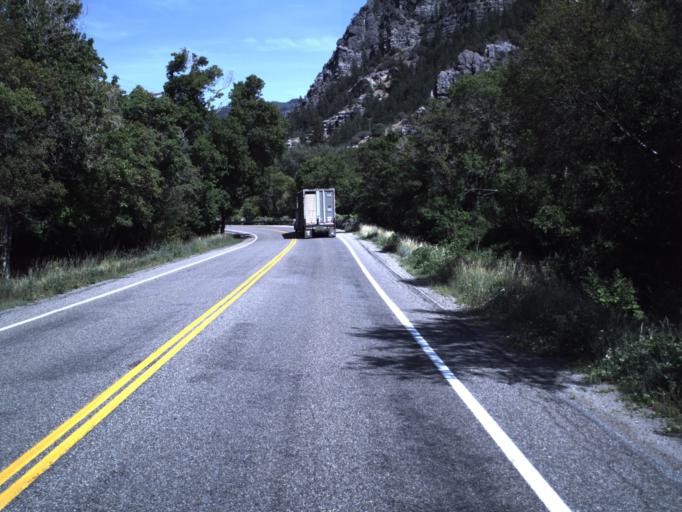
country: US
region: Utah
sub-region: Cache County
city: North Logan
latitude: 41.7440
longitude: -111.7564
